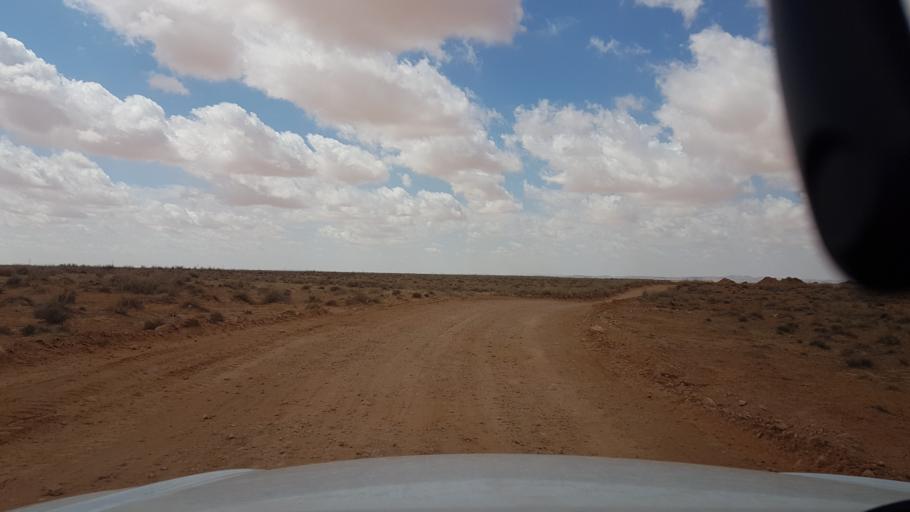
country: TN
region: Madanin
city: Medenine
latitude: 33.2713
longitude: 10.5888
